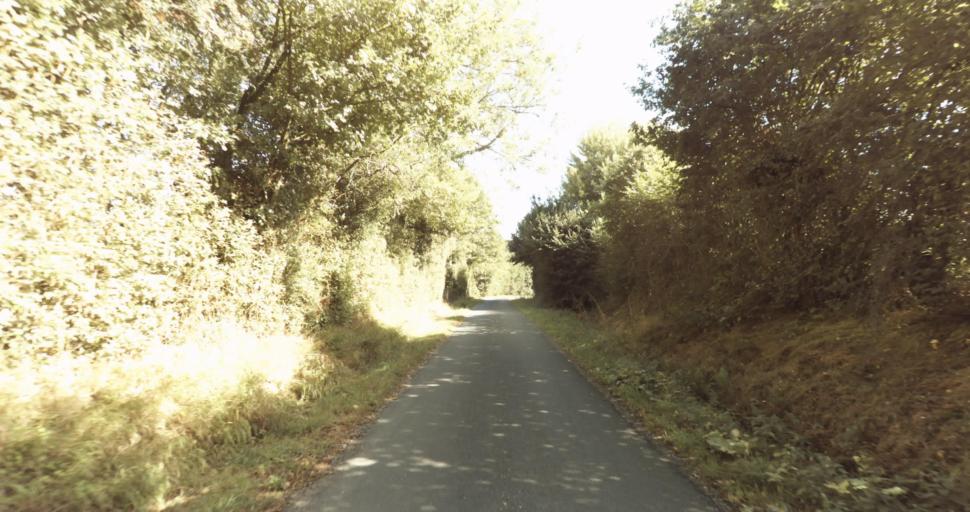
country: FR
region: Lower Normandy
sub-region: Departement de l'Orne
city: Vimoutiers
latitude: 48.9055
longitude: 0.1620
